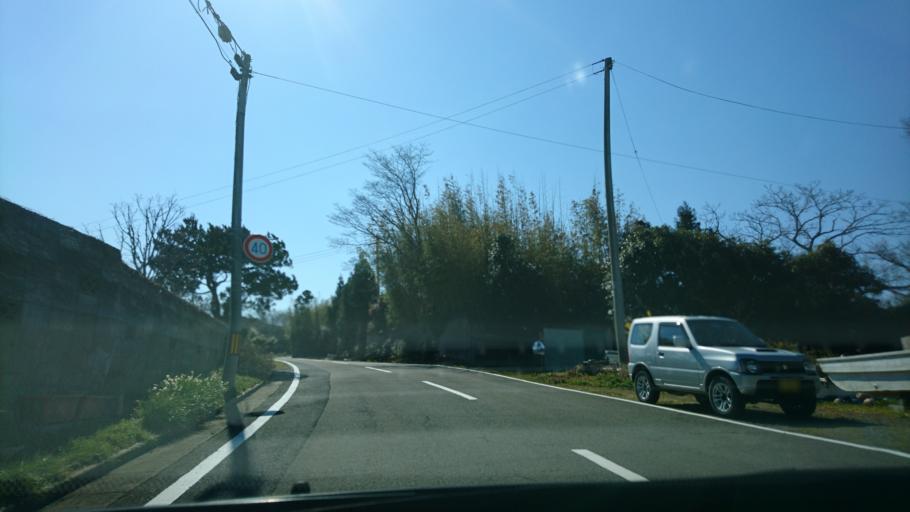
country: JP
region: Iwate
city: Ofunato
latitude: 38.8499
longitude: 141.6137
